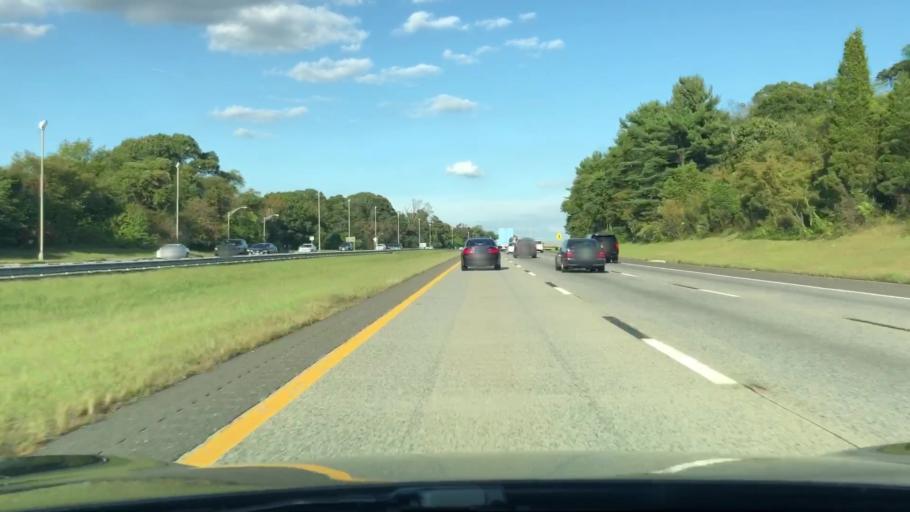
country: US
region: New Jersey
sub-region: Burlington County
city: Willingboro
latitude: 39.9897
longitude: -74.8819
